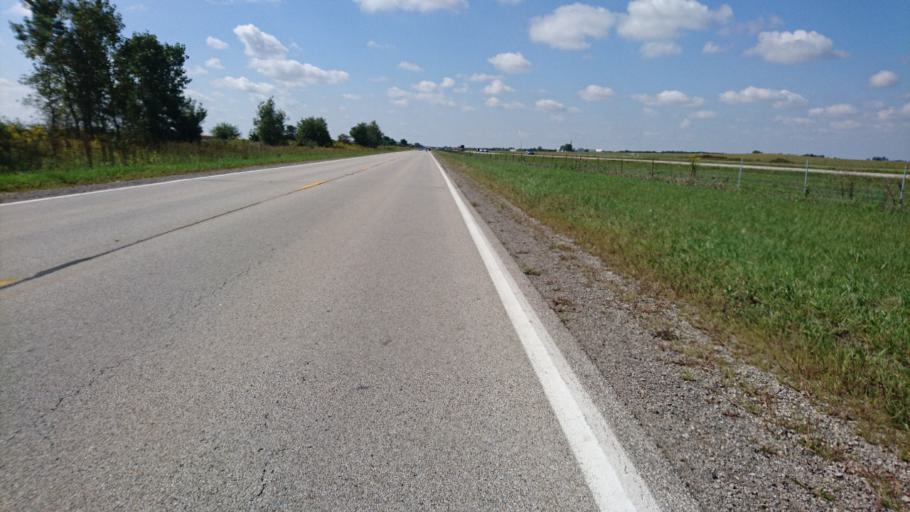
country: US
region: Illinois
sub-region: McLean County
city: Lexington
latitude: 40.6169
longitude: -88.8213
